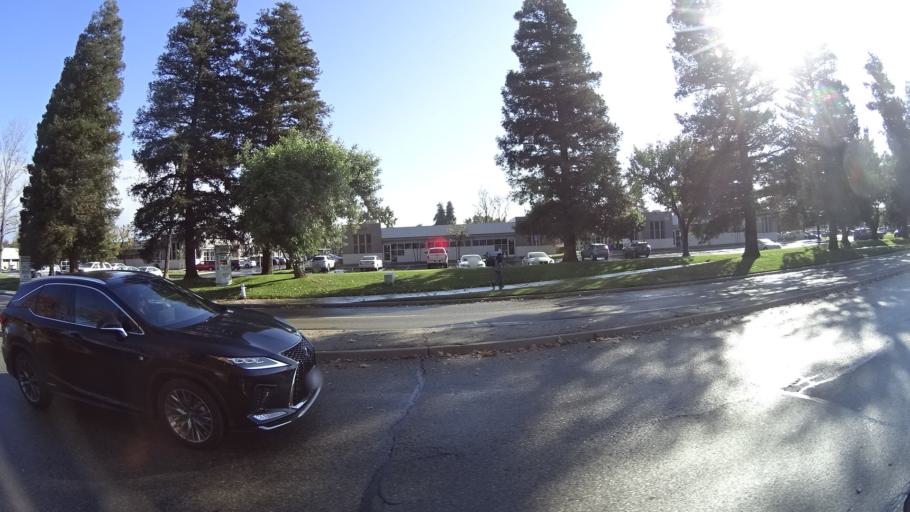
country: US
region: California
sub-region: Kern County
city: Greenacres
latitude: 35.3628
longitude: -119.0724
